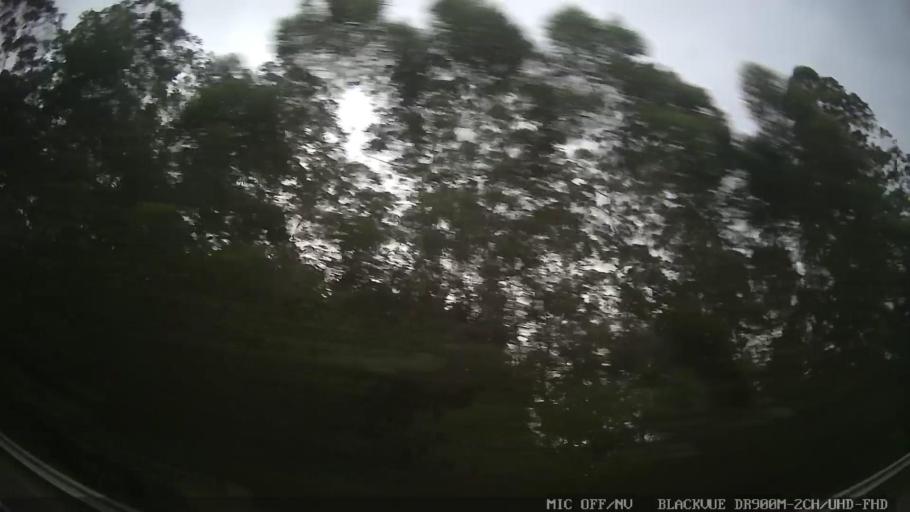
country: BR
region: Sao Paulo
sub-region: Itatiba
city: Itatiba
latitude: -22.9166
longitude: -46.7851
